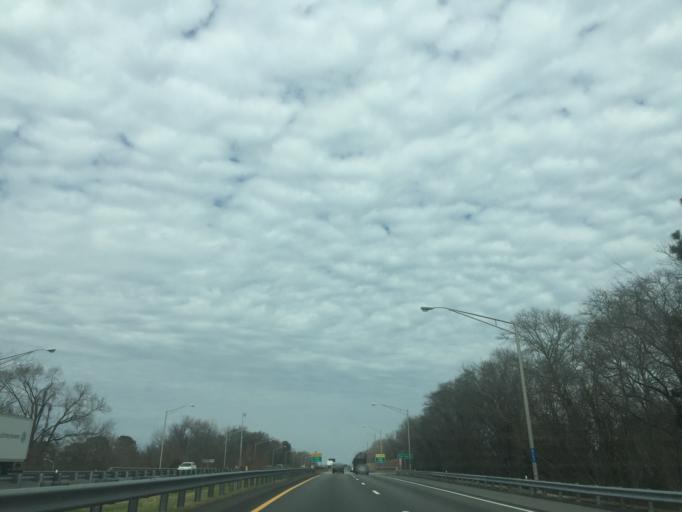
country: US
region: Virginia
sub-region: City of Norfolk
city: Norfolk
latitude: 36.9458
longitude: -76.2665
